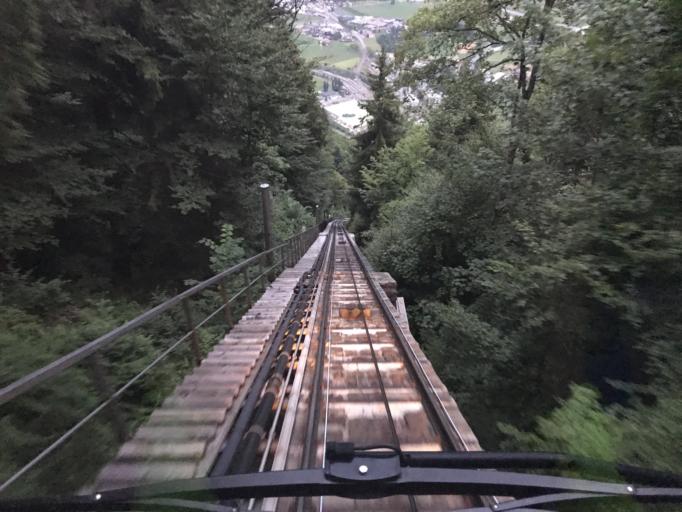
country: CH
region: Bern
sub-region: Interlaken-Oberhasli District
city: Interlaken
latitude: 46.6971
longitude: 7.8594
